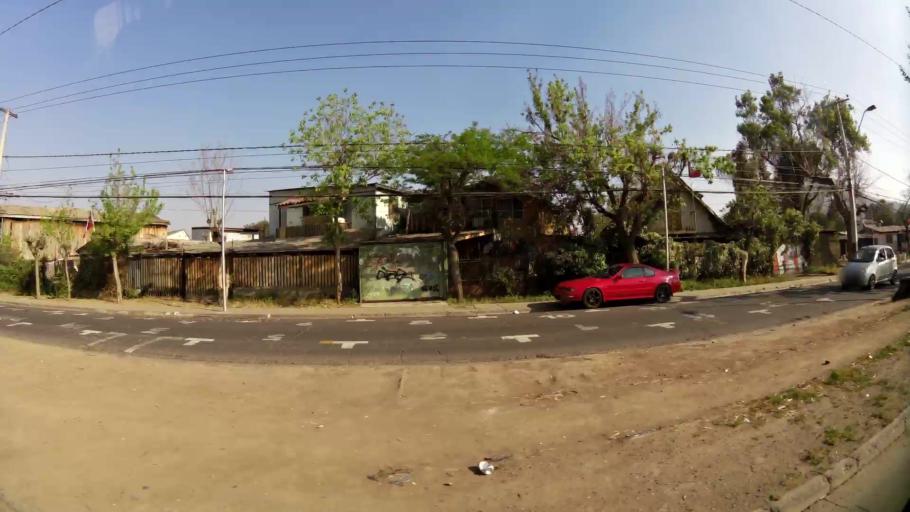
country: CL
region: Santiago Metropolitan
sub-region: Provincia de Santiago
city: Lo Prado
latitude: -33.3741
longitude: -70.6898
